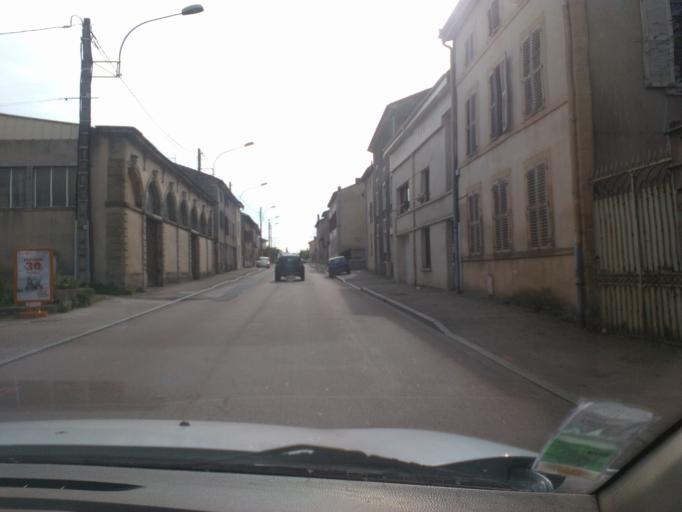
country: FR
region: Lorraine
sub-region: Departement des Vosges
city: Rambervillers
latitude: 48.3457
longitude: 6.6392
